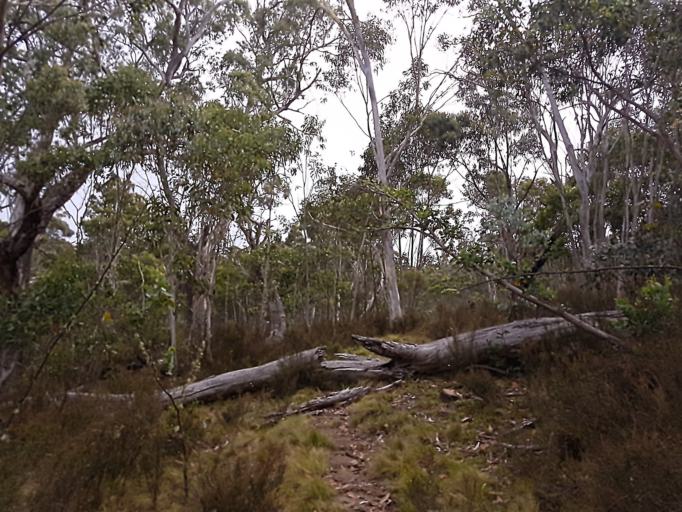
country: AU
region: New South Wales
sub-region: Snowy River
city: Jindabyne
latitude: -36.8042
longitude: 148.1868
